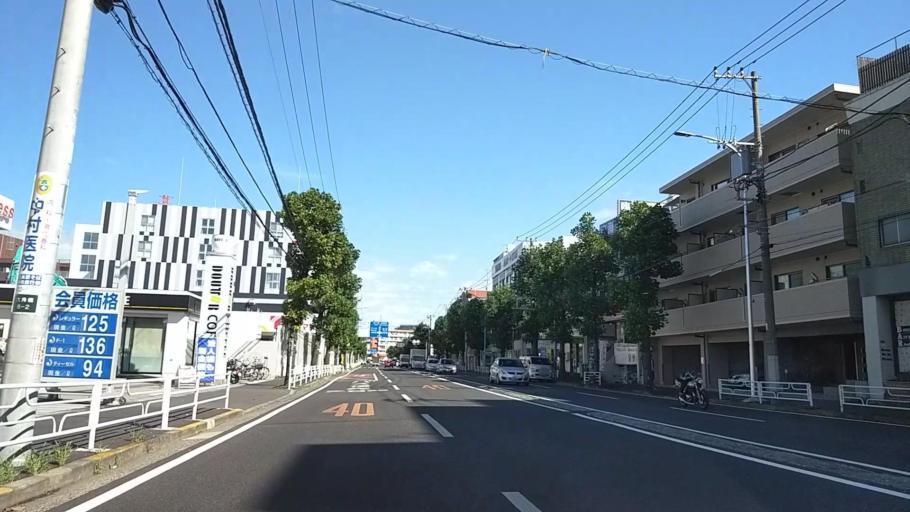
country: JP
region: Kanagawa
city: Yokohama
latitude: 35.4913
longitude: 139.6208
